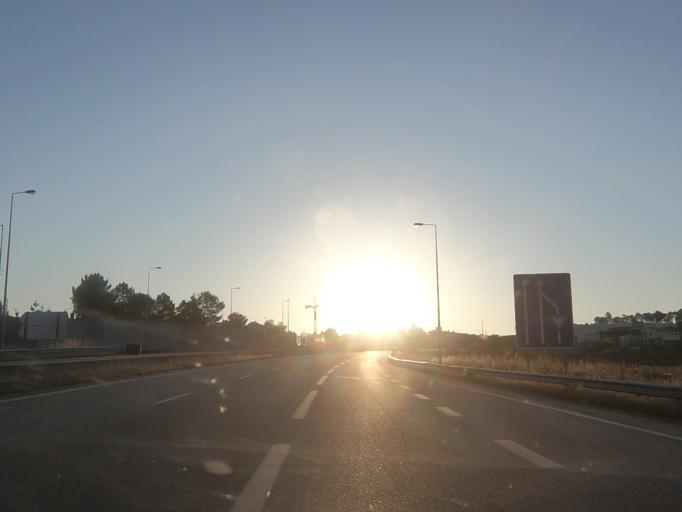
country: PT
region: Viseu
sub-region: Viseu
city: Rio de Loba
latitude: 40.6388
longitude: -7.8521
